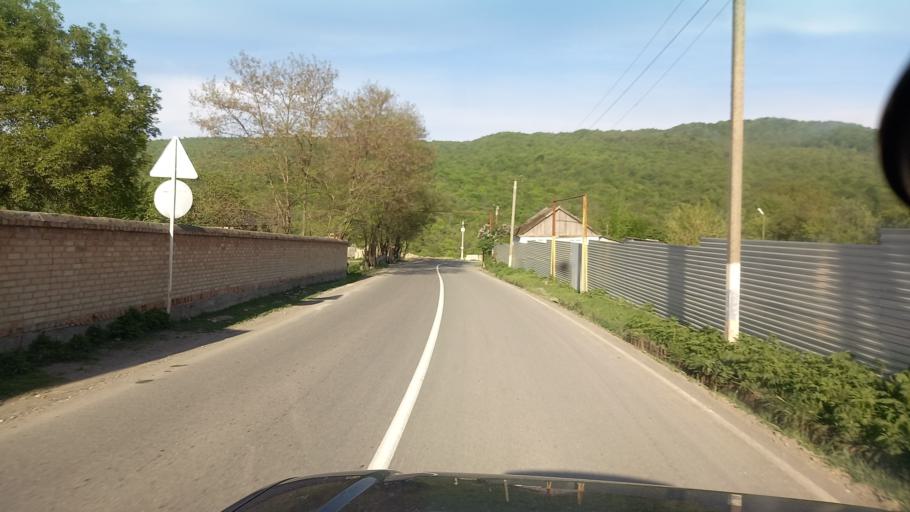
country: RU
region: Ingushetiya
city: Galashki
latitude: 43.0773
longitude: 44.9855
